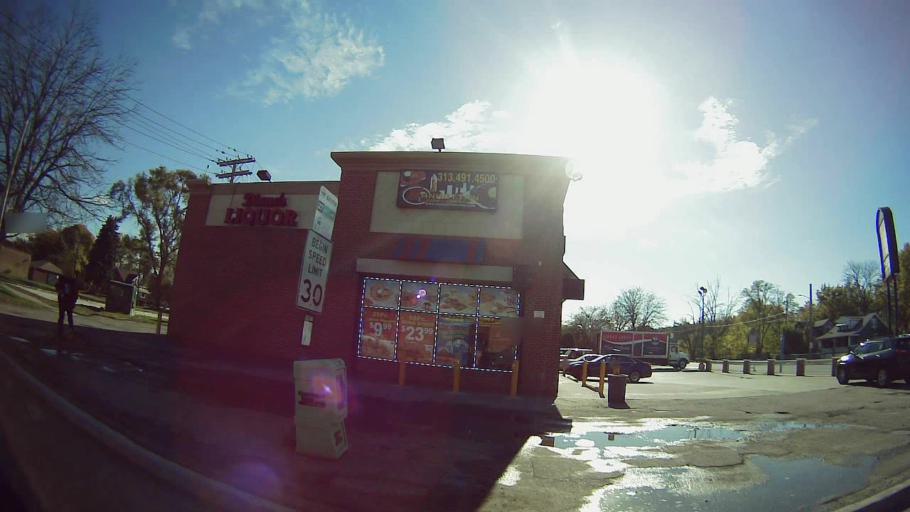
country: US
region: Michigan
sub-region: Wayne County
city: Dearborn
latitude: 42.3585
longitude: -83.1785
